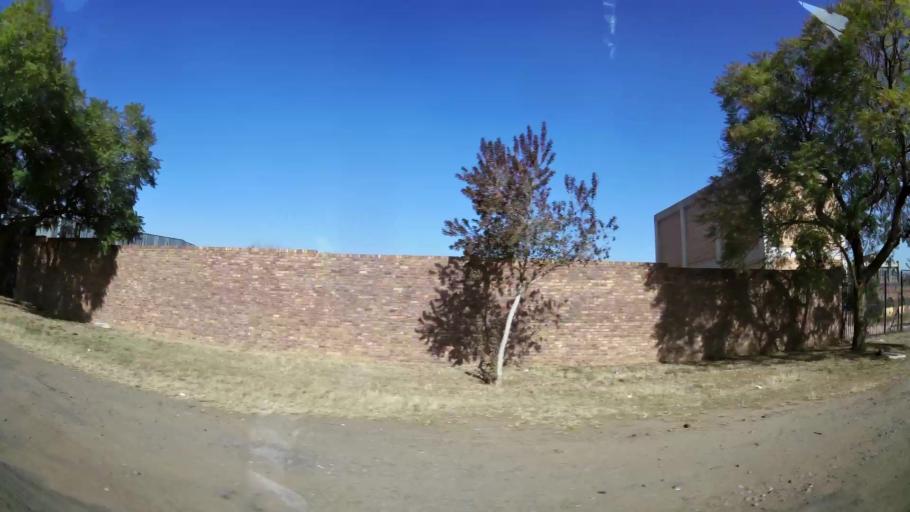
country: ZA
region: Gauteng
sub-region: City of Tshwane Metropolitan Municipality
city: Pretoria
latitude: -25.7159
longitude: 28.2491
